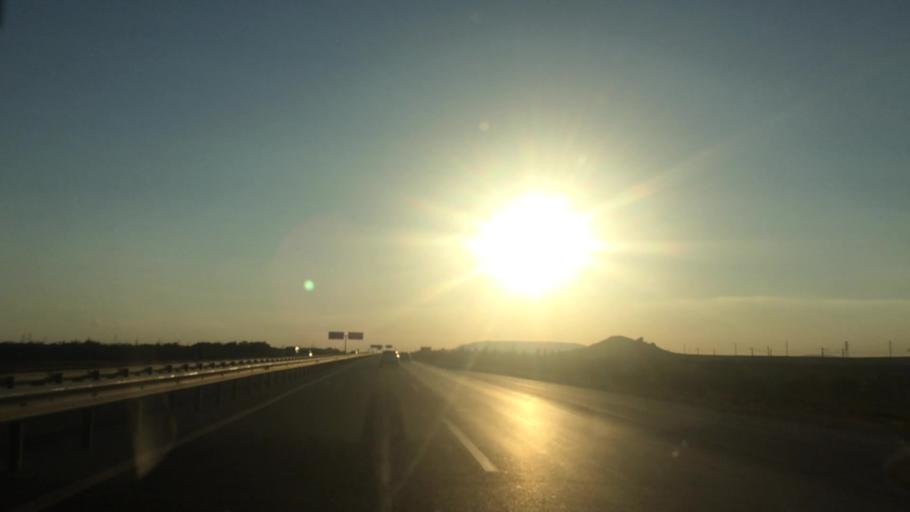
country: AZ
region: Baki
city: Qobustan
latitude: 39.9535
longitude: 49.3768
